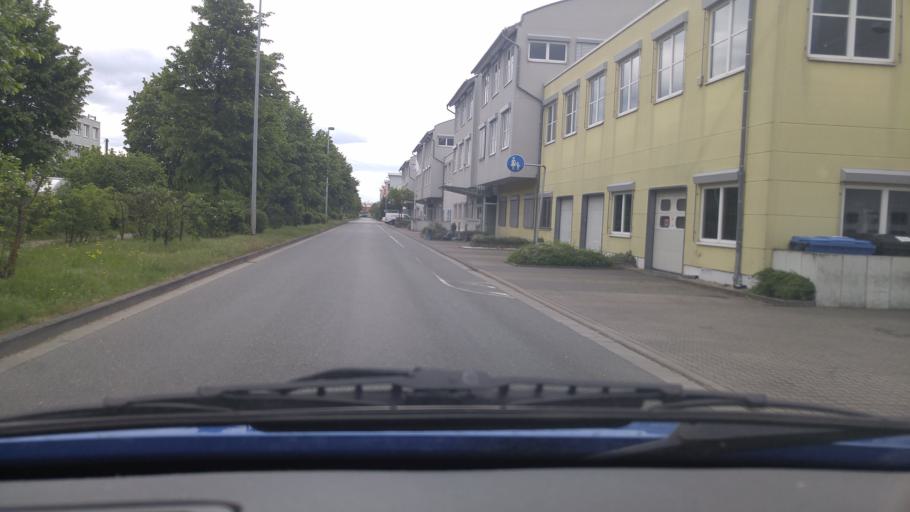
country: DE
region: Hesse
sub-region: Regierungsbezirk Darmstadt
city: Ginsheim-Gustavsburg
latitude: 49.9882
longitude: 8.3163
